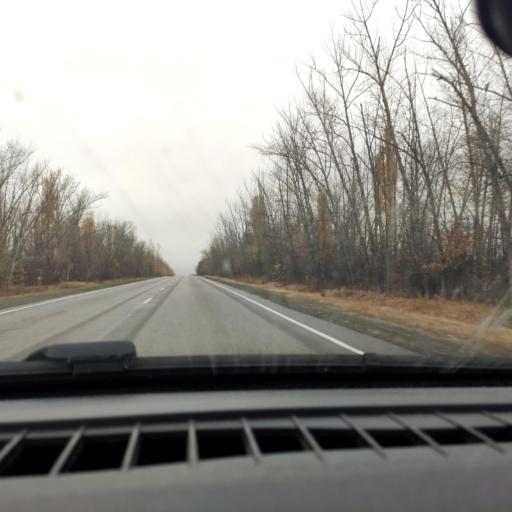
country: RU
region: Voronezj
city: Ostrogozhsk
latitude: 51.0134
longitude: 38.9900
